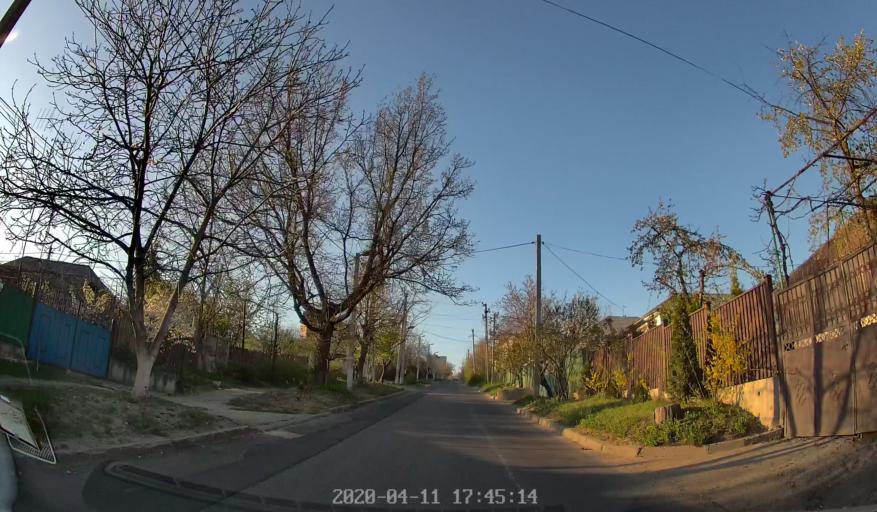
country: MD
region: Chisinau
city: Chisinau
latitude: 46.9833
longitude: 28.8228
